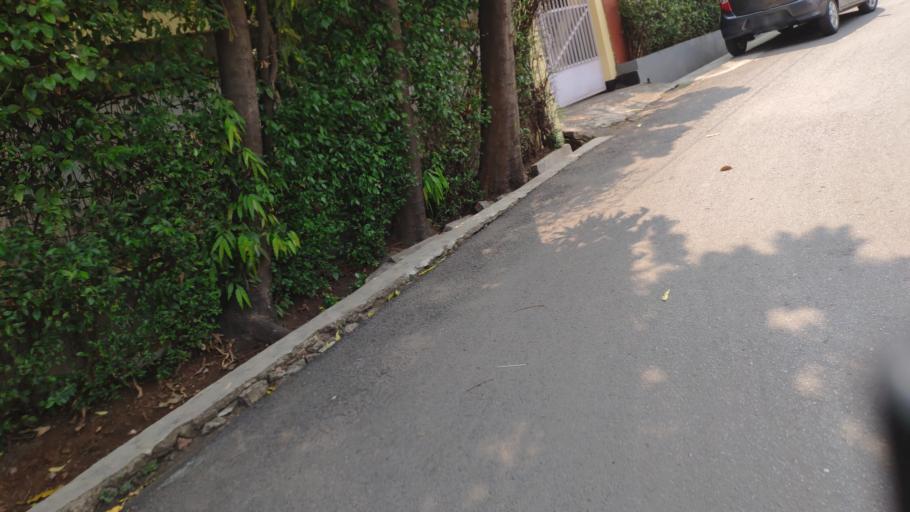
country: ID
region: Jakarta Raya
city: Jakarta
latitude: -6.3068
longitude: 106.8287
